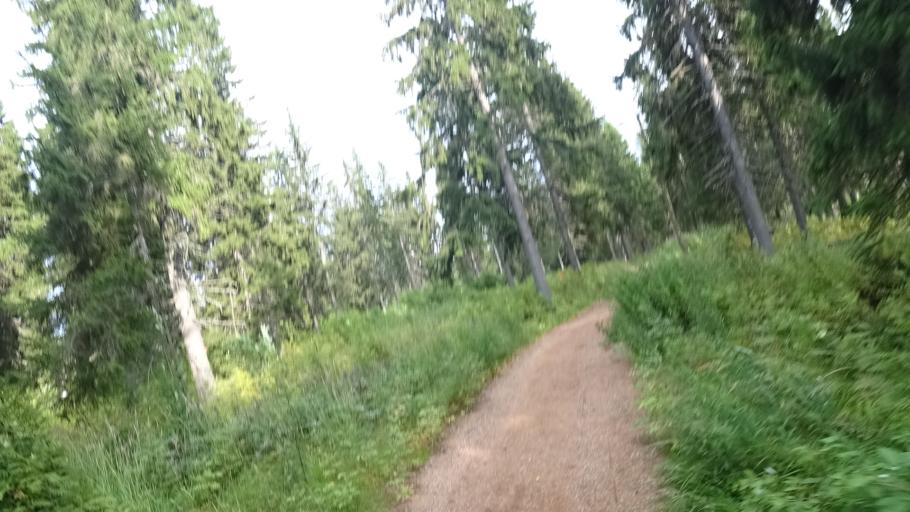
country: FI
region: North Karelia
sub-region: Joensuu
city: Ilomantsi
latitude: 62.6676
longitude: 30.9093
